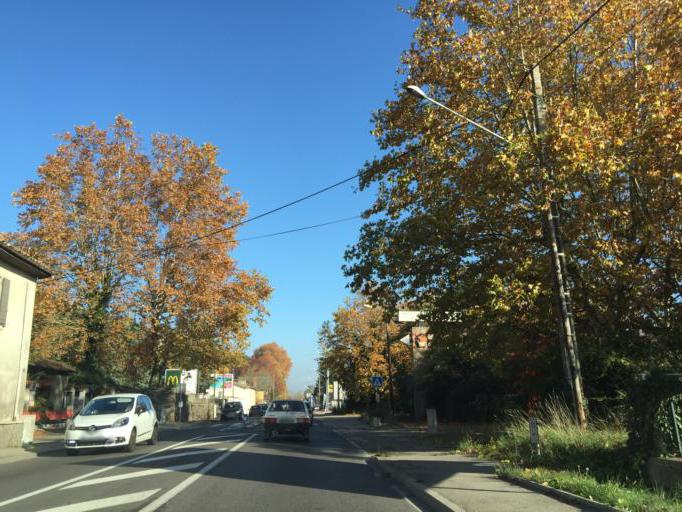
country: FR
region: Rhone-Alpes
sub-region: Departement du Rhone
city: Brignais
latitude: 45.6557
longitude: 4.7510
